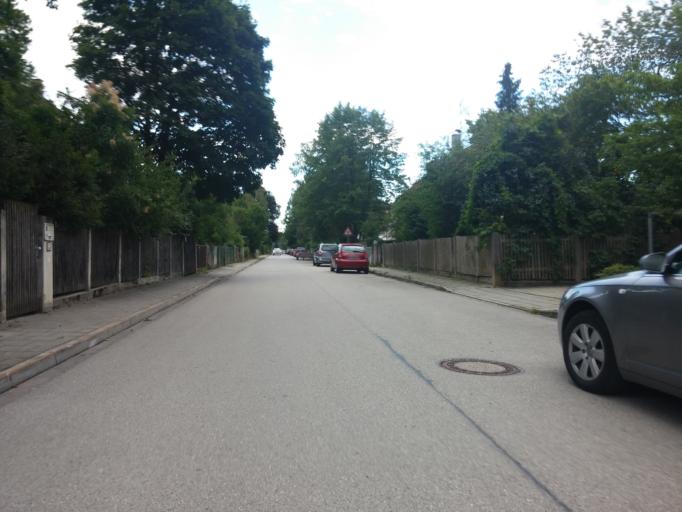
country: DE
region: Bavaria
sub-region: Upper Bavaria
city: Haar
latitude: 48.1083
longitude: 11.7425
